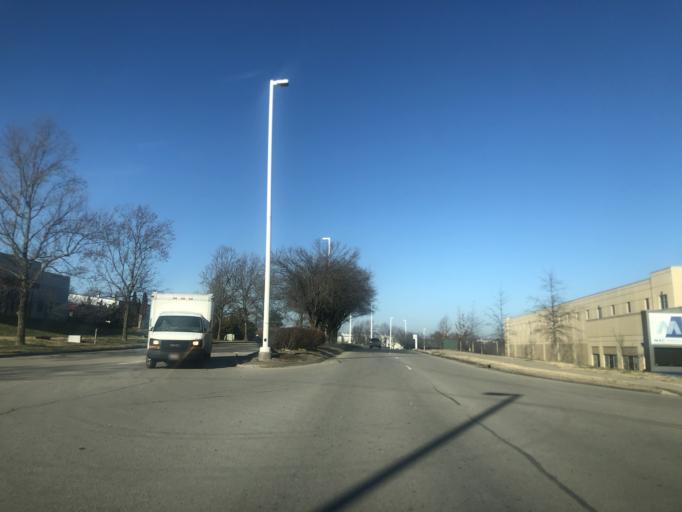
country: US
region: Tennessee
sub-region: Rutherford County
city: La Vergne
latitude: 36.0375
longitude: -86.6431
